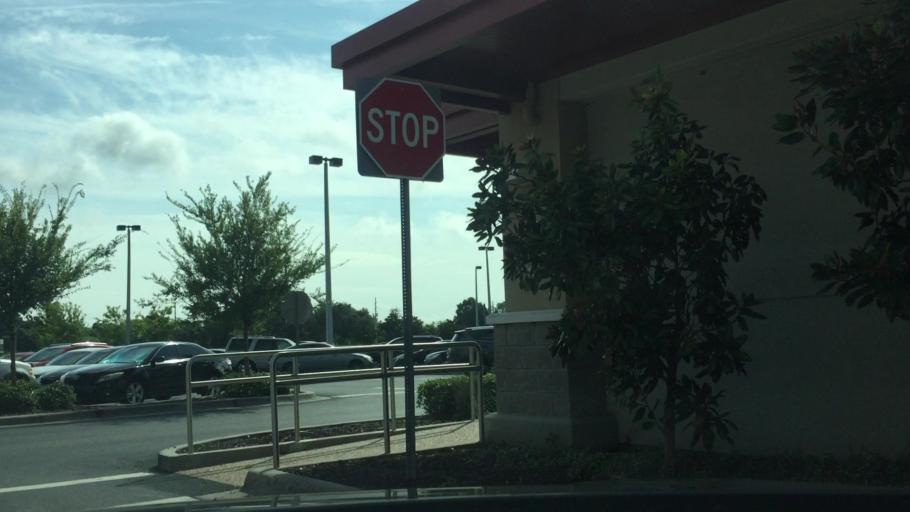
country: US
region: Florida
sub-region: Osceola County
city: Buenaventura Lakes
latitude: 28.2798
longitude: -81.3478
